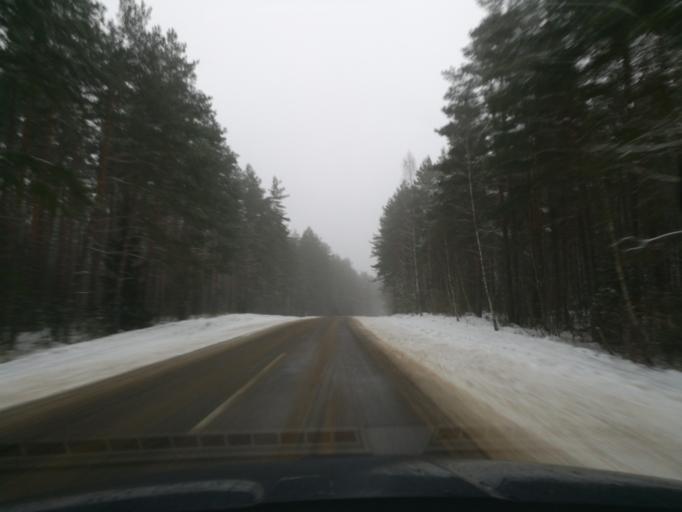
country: LT
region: Utenos apskritis
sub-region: Anyksciai
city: Anyksciai
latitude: 55.4619
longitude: 25.0435
